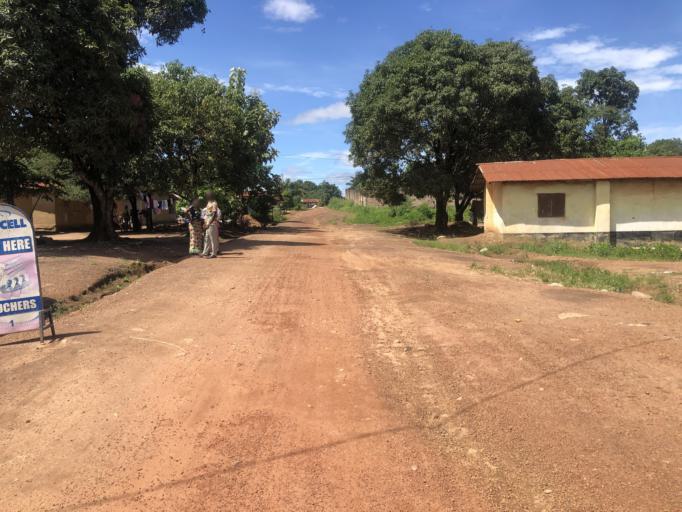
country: SL
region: Eastern Province
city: Koidu
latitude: 8.6383
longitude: -10.9536
